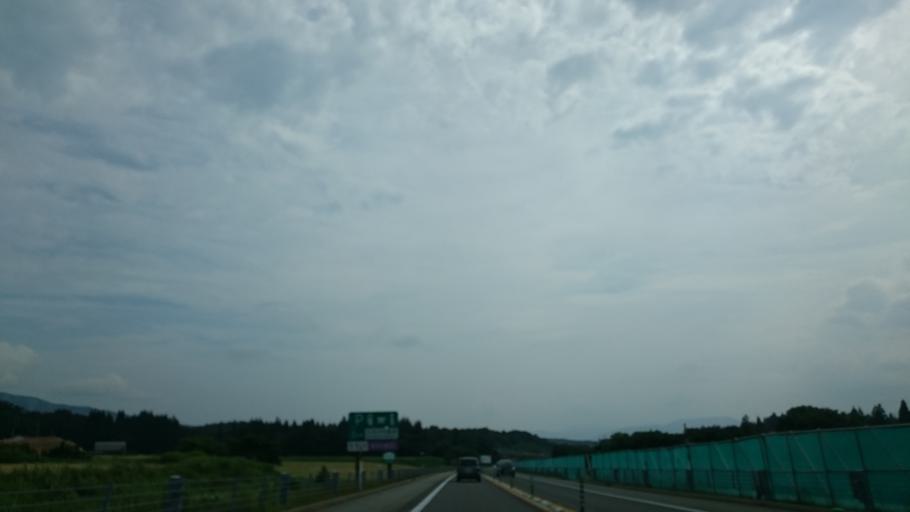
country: JP
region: Gifu
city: Gujo
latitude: 36.0016
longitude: 136.9269
